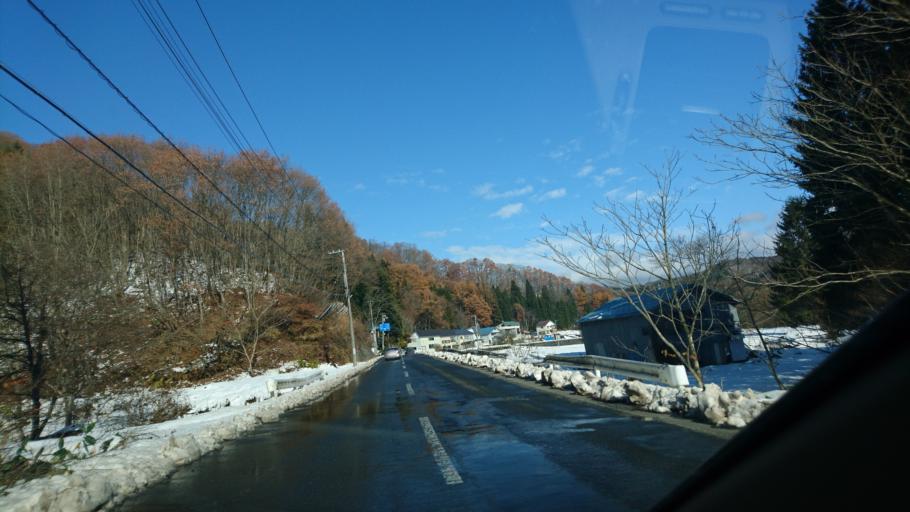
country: JP
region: Akita
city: Yokotemachi
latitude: 39.3435
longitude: 140.7620
